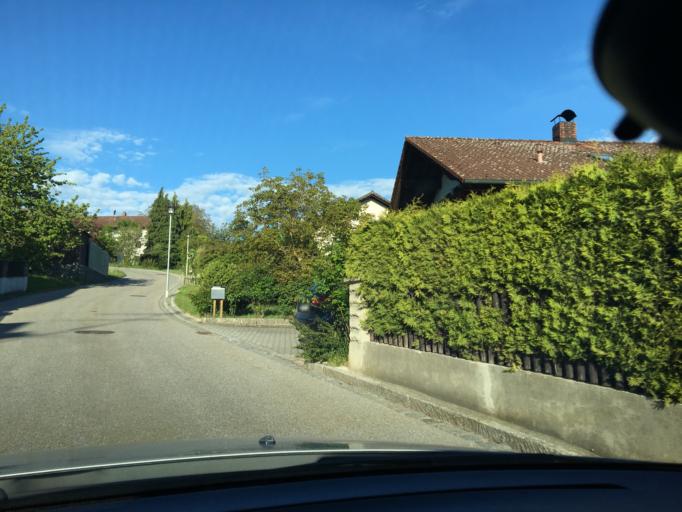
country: DE
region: Bavaria
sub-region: Lower Bavaria
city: Schalkham
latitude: 48.4941
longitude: 12.3736
